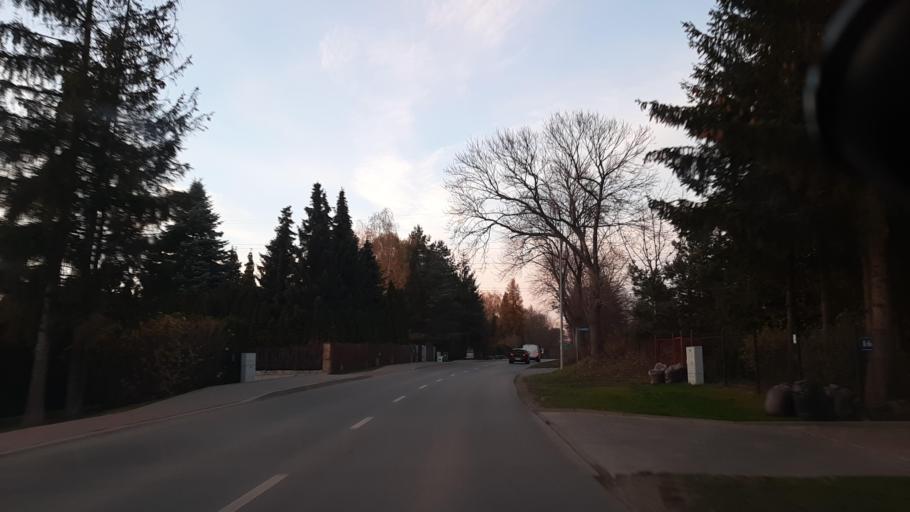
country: PL
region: Lublin Voivodeship
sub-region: Powiat lubelski
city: Jastkow
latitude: 51.2850
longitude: 22.4994
